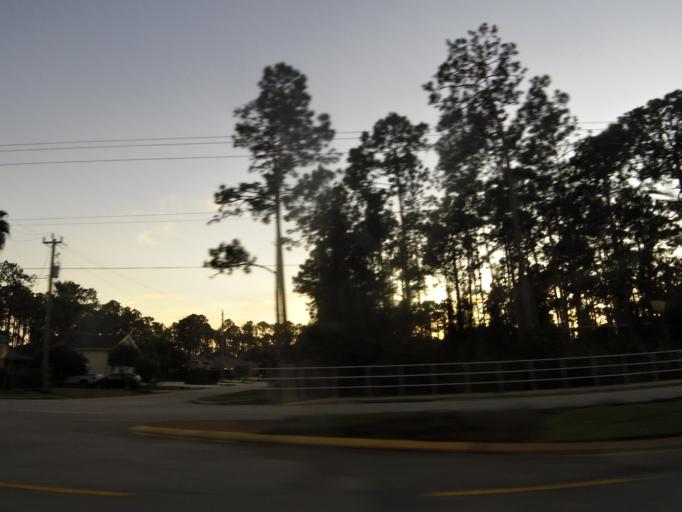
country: US
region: Florida
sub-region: Flagler County
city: Palm Coast
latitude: 29.5660
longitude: -81.2454
